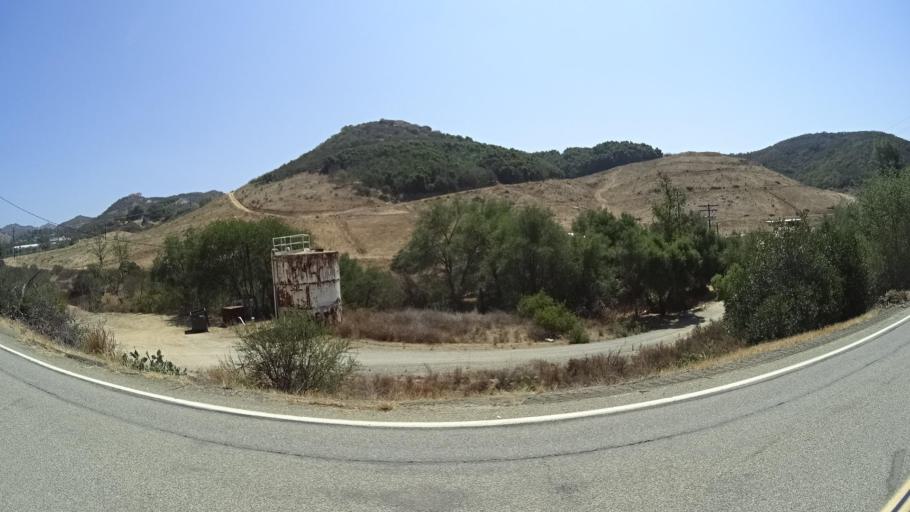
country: US
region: California
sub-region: San Diego County
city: Fallbrook
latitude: 33.4189
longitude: -117.3095
